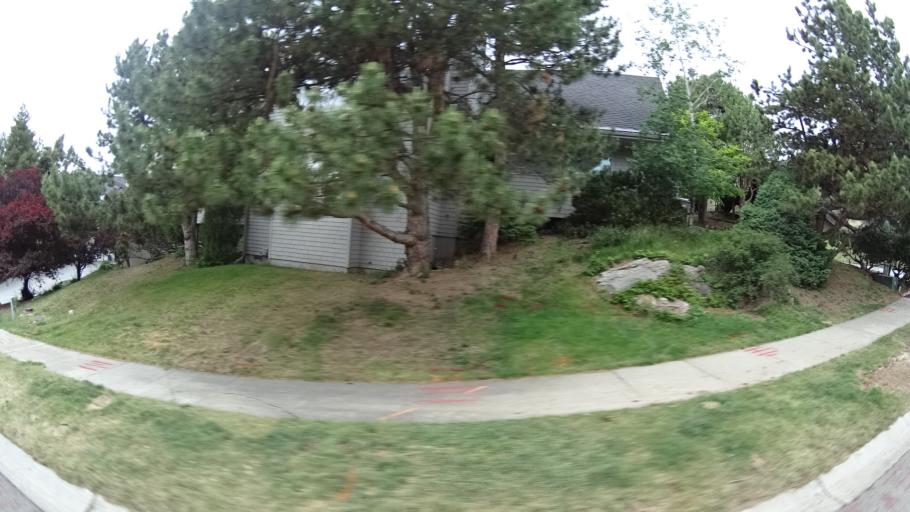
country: US
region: Idaho
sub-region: Ada County
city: Boise
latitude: 43.6132
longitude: -116.1697
